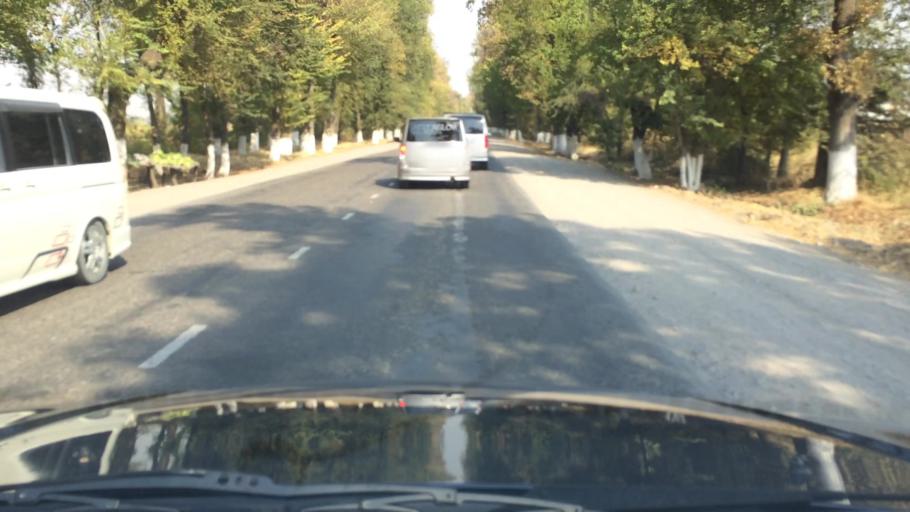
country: KG
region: Chuy
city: Lebedinovka
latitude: 42.9158
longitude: 74.6887
